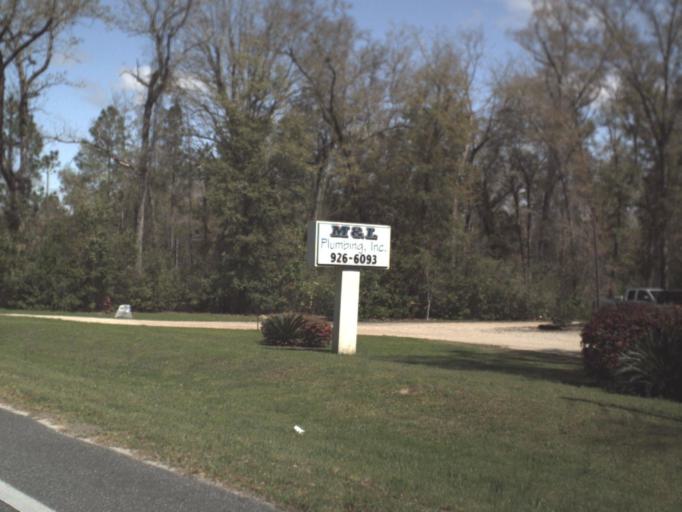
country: US
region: Florida
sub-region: Wakulla County
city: Crawfordville
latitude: 30.1200
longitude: -84.3841
